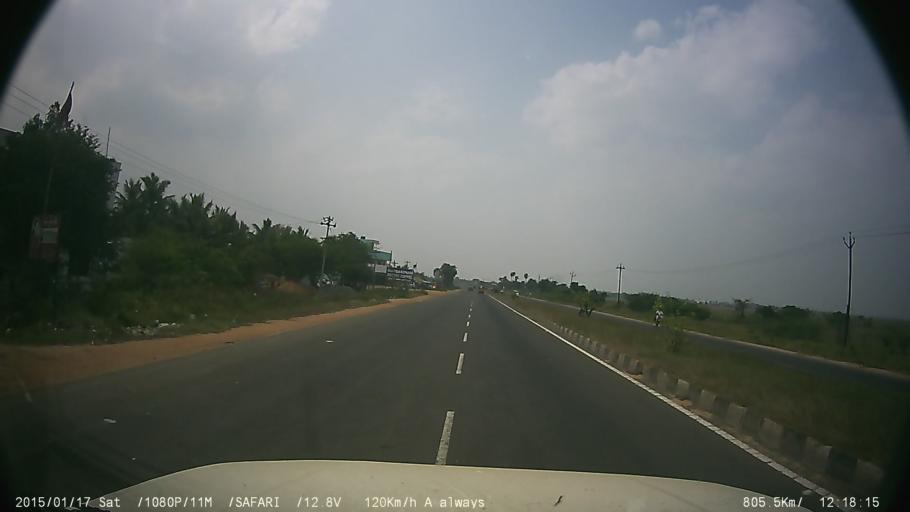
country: IN
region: Tamil Nadu
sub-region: Kancheepuram
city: Wallajahbad
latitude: 12.9074
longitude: 79.8317
